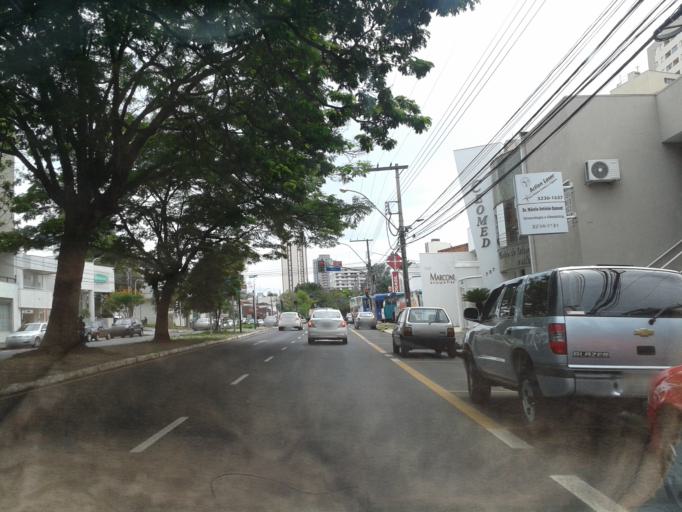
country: BR
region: Minas Gerais
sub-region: Uberlandia
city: Uberlandia
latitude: -18.9200
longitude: -48.2852
